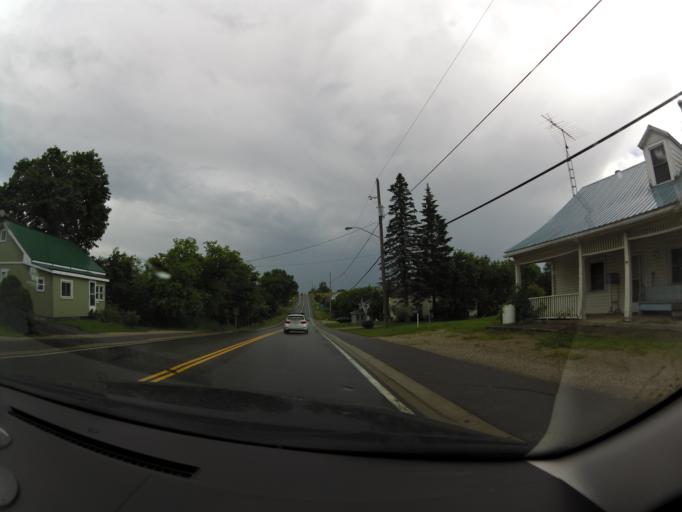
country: CA
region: Ontario
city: Perth
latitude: 45.0820
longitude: -76.4447
